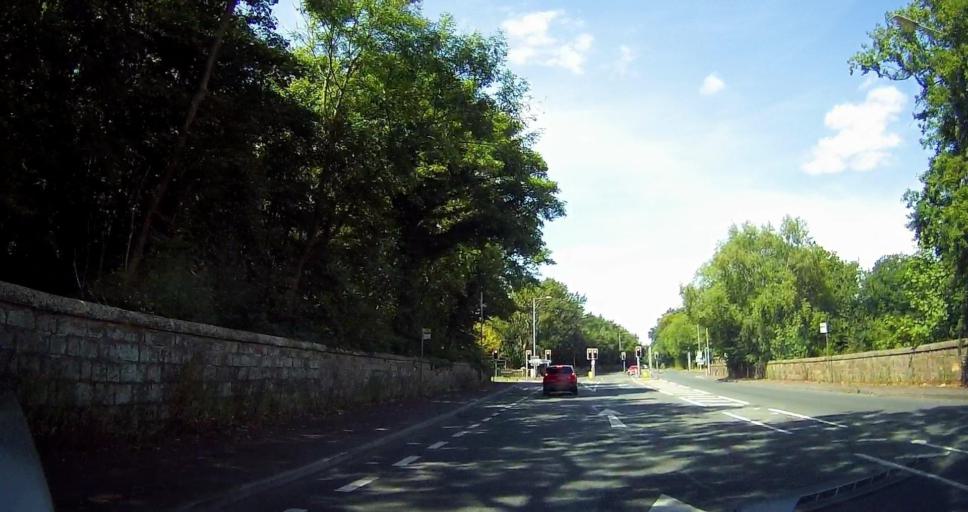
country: GB
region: England
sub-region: Staffordshire
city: Codsall
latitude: 52.6111
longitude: -2.2037
